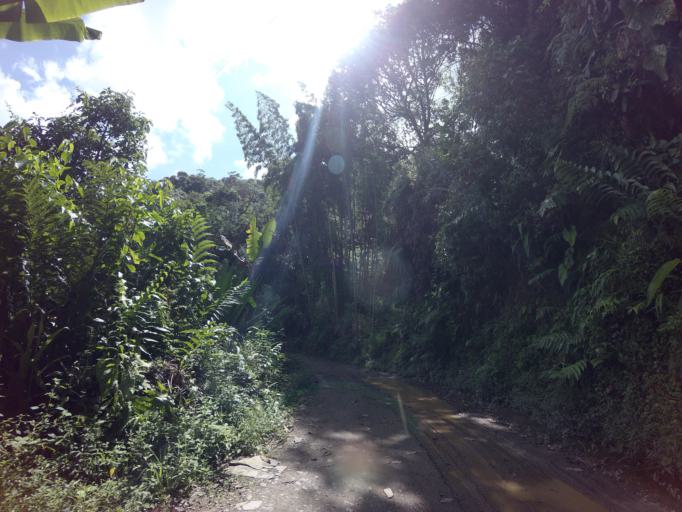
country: CO
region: Antioquia
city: Narino
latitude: 5.5167
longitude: -75.1768
